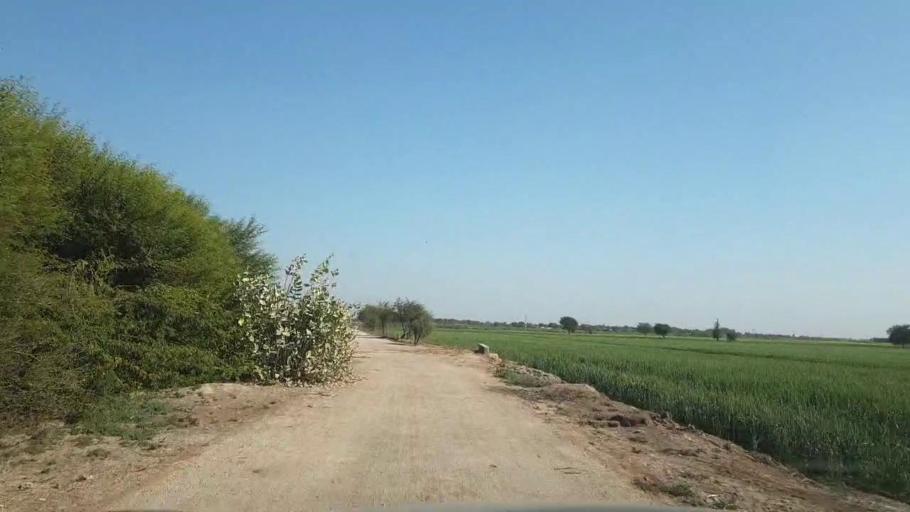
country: PK
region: Sindh
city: Tando Adam
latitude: 25.6654
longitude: 68.6941
